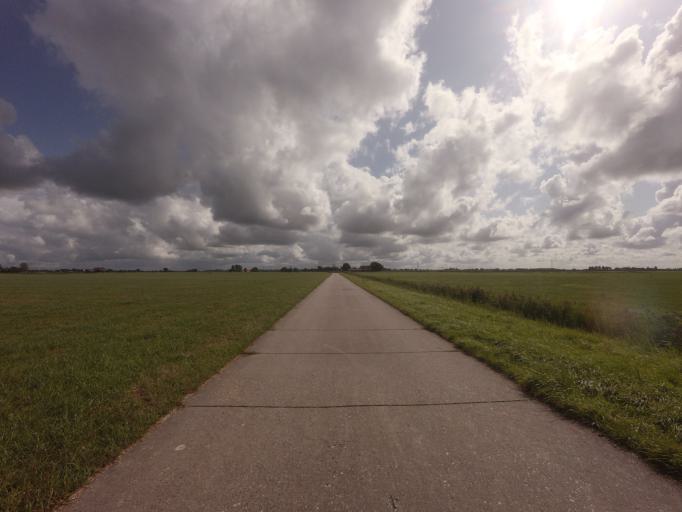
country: NL
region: Friesland
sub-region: Sudwest Fryslan
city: Scharnegoutum
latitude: 53.0687
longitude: 5.6389
